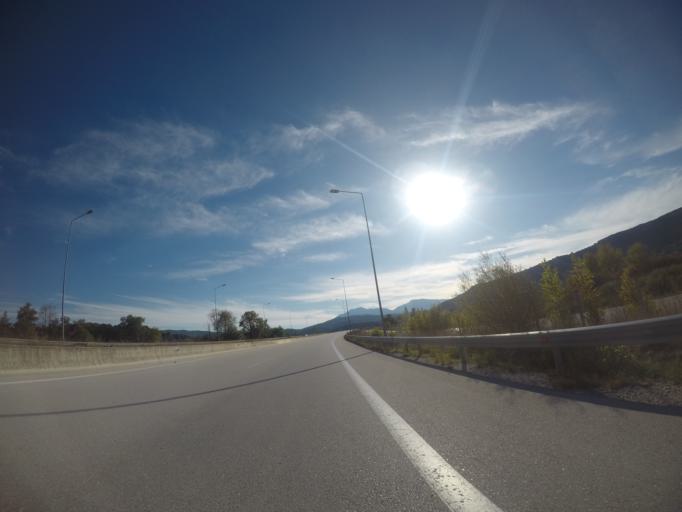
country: GR
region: Epirus
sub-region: Nomos Ioanninon
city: Koutselio
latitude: 39.6111
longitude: 20.9409
